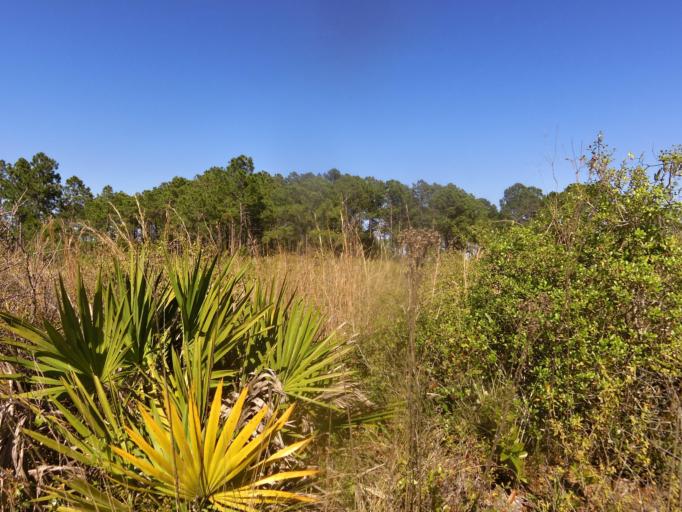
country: US
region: Florida
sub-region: Duval County
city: Atlantic Beach
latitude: 30.4736
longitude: -81.4879
